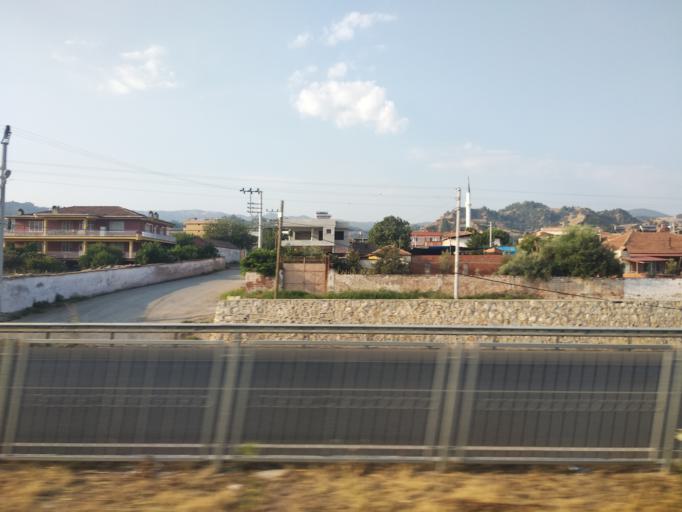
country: TR
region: Manisa
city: Ahmetli
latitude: 38.5059
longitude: 27.9992
